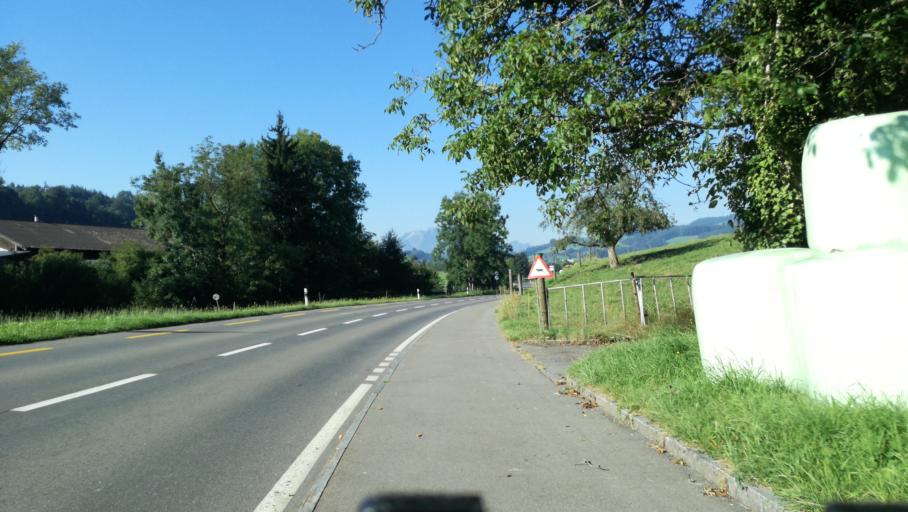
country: CH
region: Lucerne
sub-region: Lucerne-Land District
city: Meierskappel
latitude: 47.1169
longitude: 8.4621
